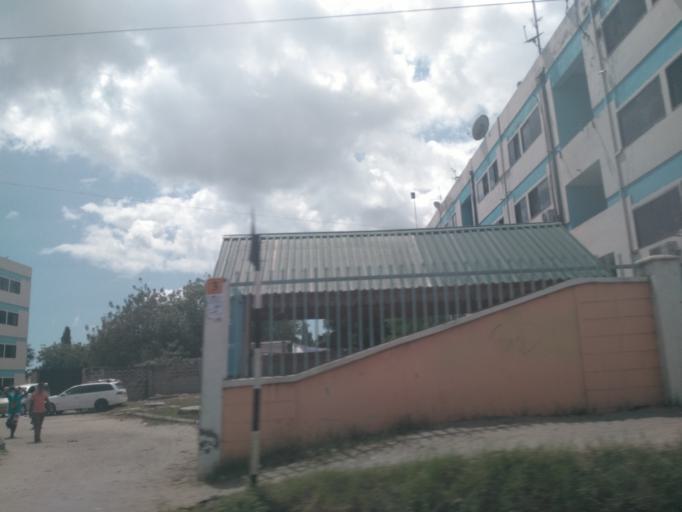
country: TZ
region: Dar es Salaam
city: Dar es Salaam
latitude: -6.8254
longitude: 39.2619
